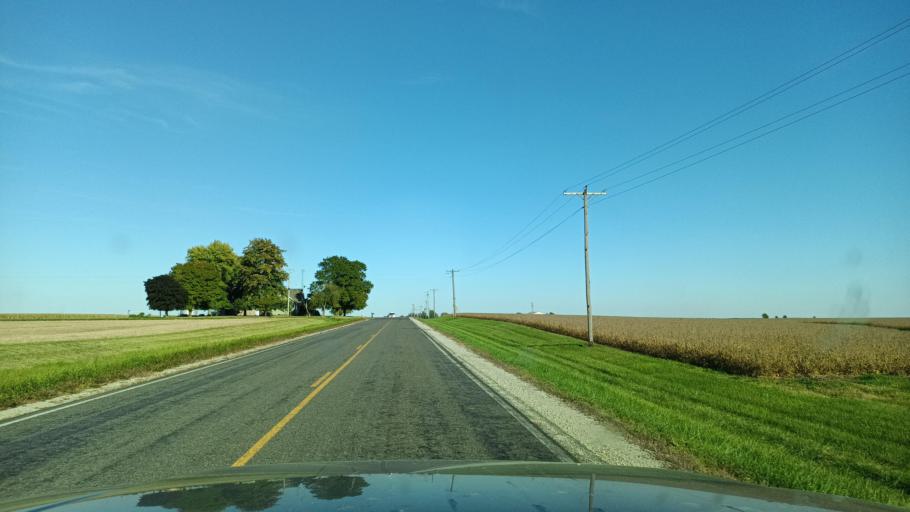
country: US
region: Illinois
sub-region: De Witt County
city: Farmer City
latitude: 40.2240
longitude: -88.7387
